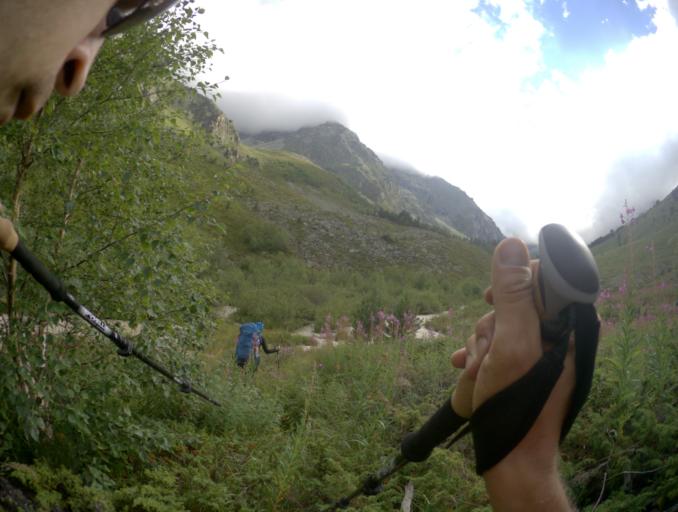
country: RU
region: Karachayevo-Cherkesiya
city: Uchkulan
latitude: 43.3399
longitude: 42.1365
